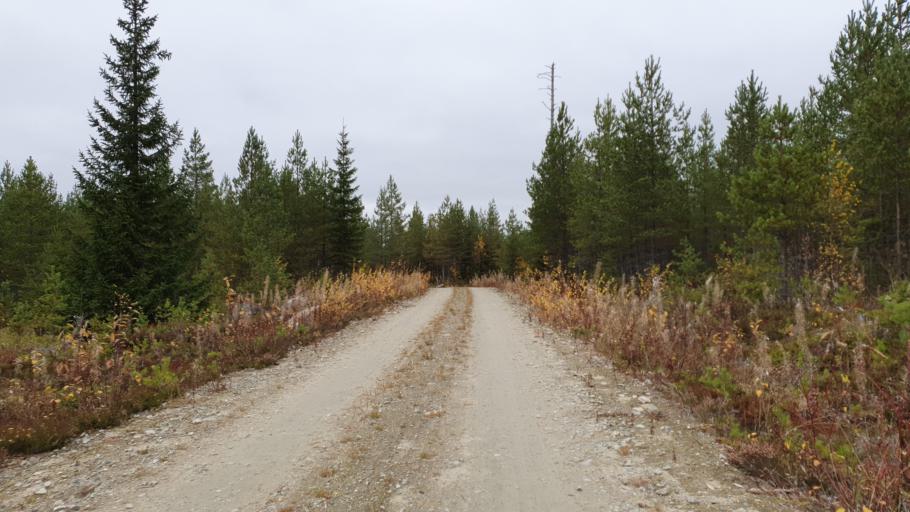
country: FI
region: Kainuu
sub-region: Kehys-Kainuu
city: Kuhmo
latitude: 64.4477
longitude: 29.6180
